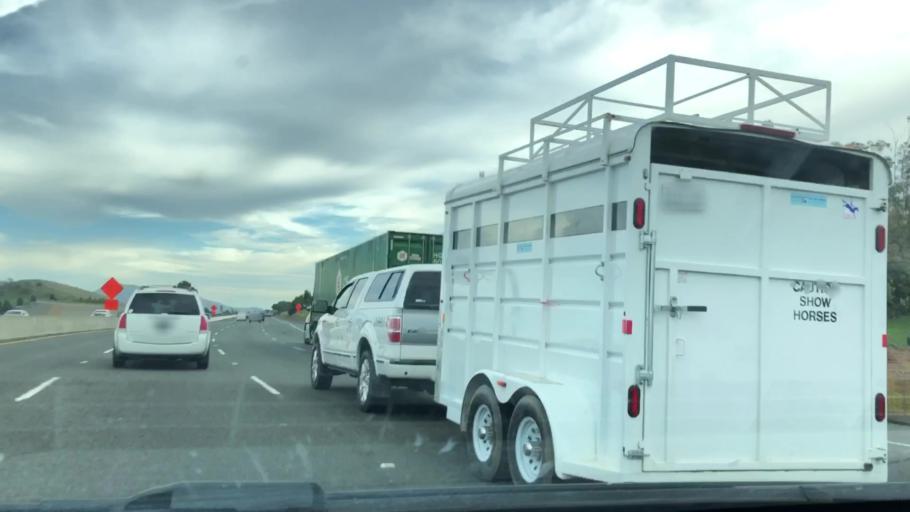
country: US
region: California
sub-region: Contra Costa County
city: Vine Hill
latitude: 38.0185
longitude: -122.0961
